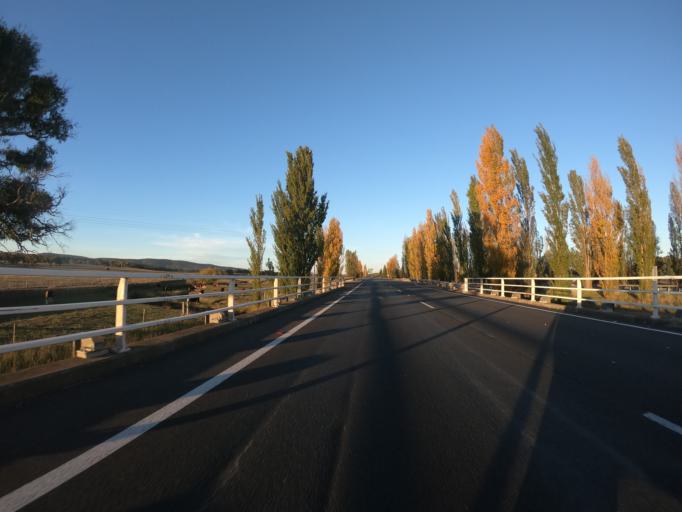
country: AU
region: New South Wales
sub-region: Goulburn Mulwaree
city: Goulburn
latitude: -34.7950
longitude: 149.6173
